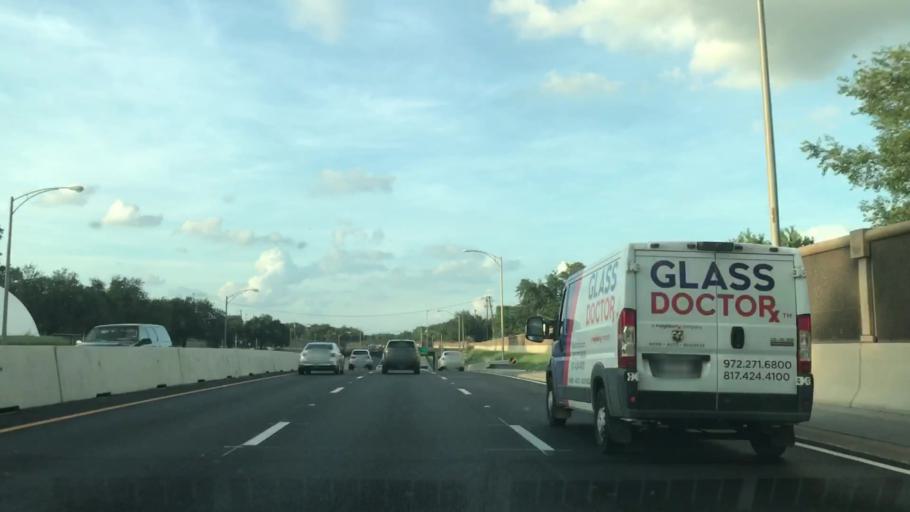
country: US
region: Texas
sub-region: Dallas County
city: University Park
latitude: 32.8847
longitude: -96.8090
